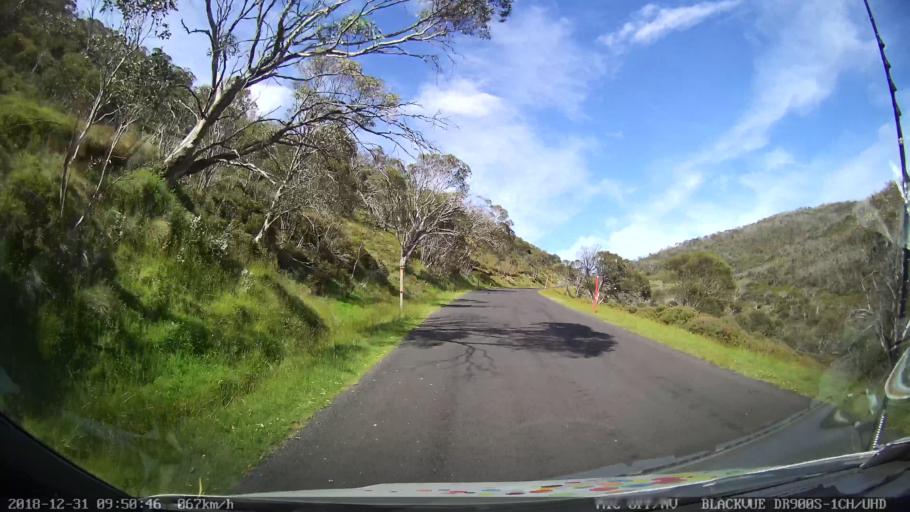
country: AU
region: New South Wales
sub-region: Snowy River
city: Jindabyne
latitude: -36.5220
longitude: 148.2695
